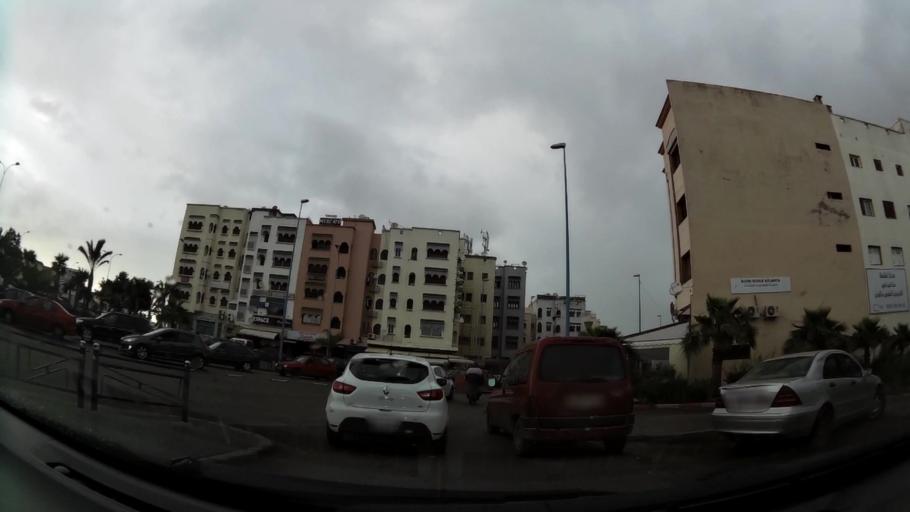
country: MA
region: Grand Casablanca
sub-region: Casablanca
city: Casablanca
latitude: 33.5514
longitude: -7.6025
